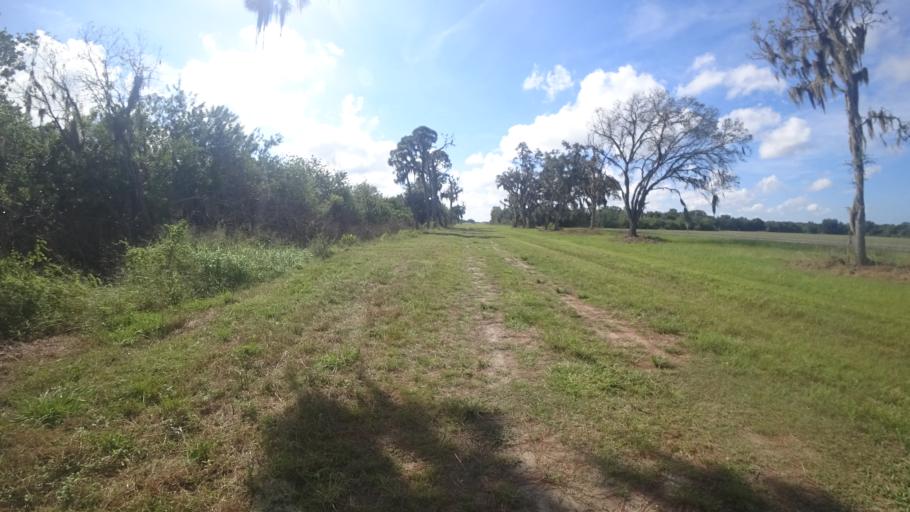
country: US
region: Florida
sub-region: Hillsborough County
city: Ruskin
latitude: 27.6436
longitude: -82.4971
